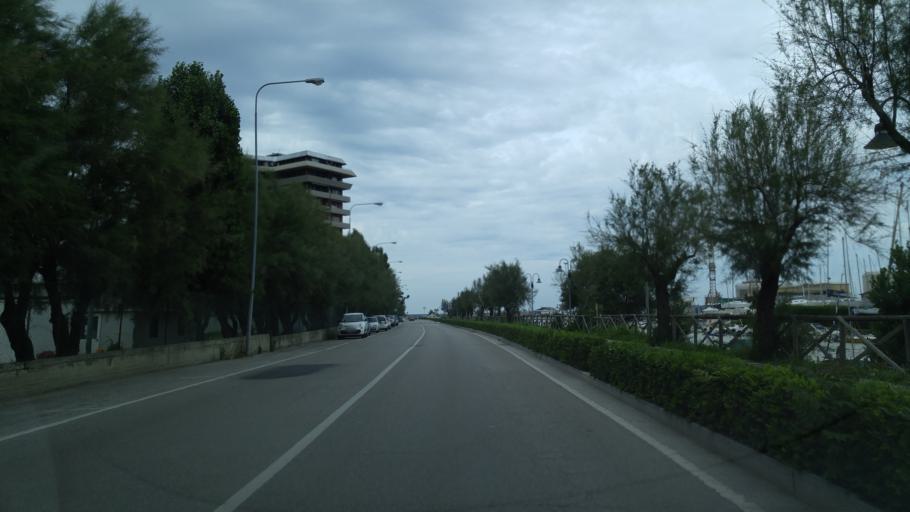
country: IT
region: The Marches
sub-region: Provincia di Pesaro e Urbino
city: Pesaro
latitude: 43.9202
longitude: 12.9024
